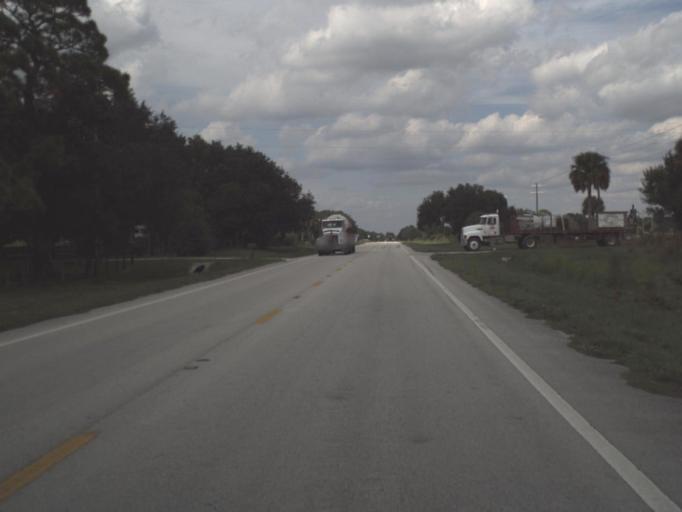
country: US
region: Florida
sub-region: Okeechobee County
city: Cypress Quarters
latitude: 27.3303
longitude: -80.8237
